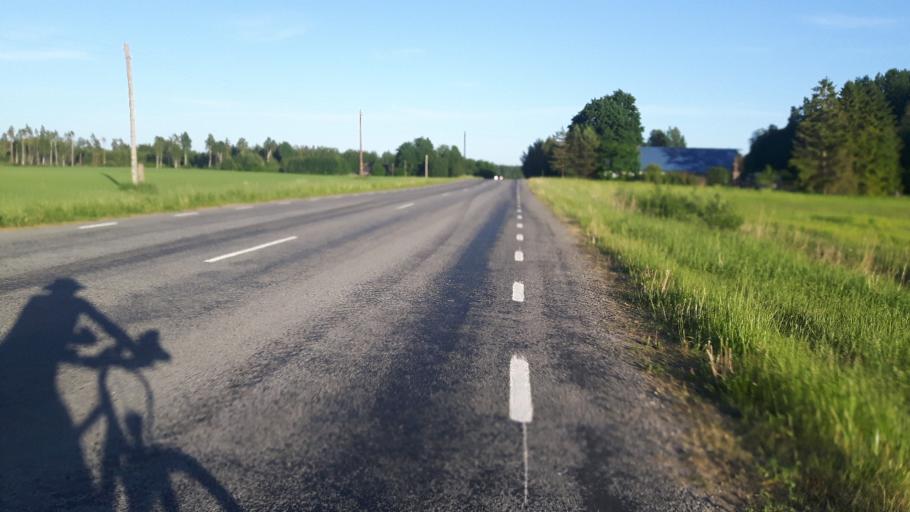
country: EE
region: Raplamaa
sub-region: Jaervakandi vald
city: Jarvakandi
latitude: 58.7851
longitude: 24.9376
